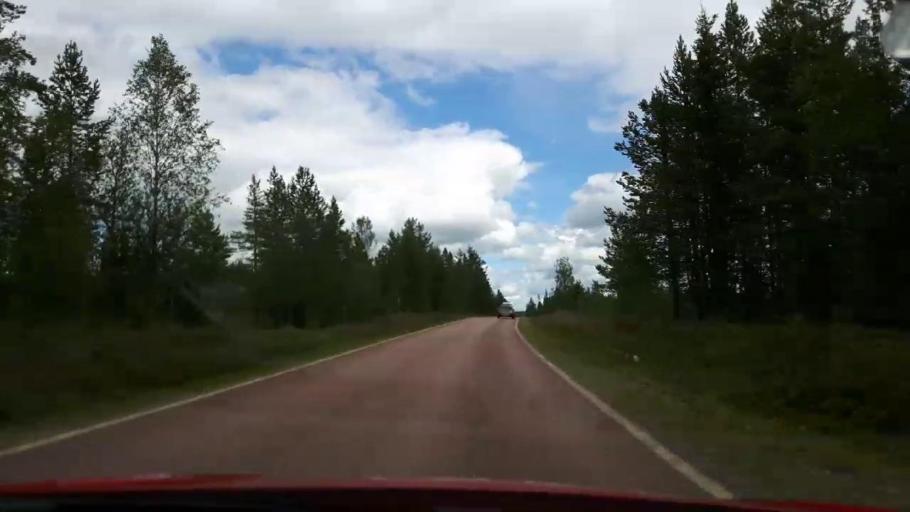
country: NO
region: Hedmark
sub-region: Trysil
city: Innbygda
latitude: 61.8805
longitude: 12.9709
